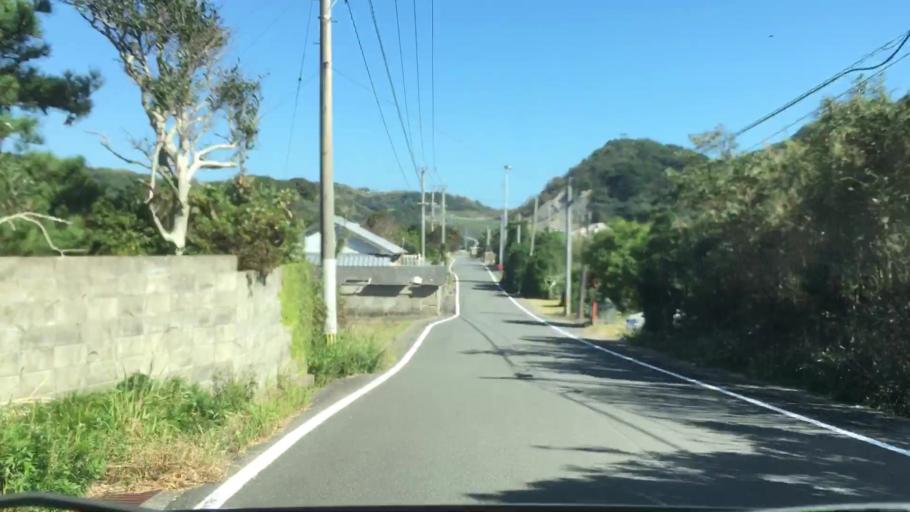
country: JP
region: Nagasaki
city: Sasebo
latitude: 33.0079
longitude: 129.5577
